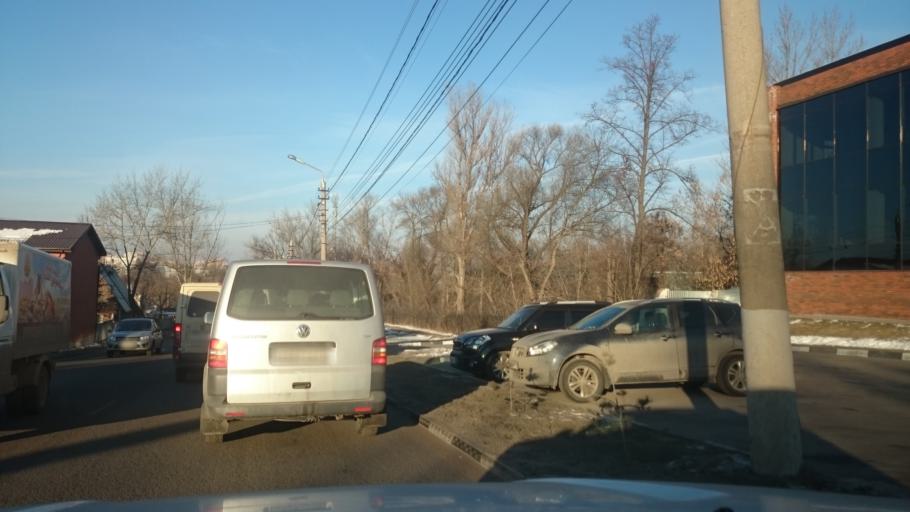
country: RU
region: Tula
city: Tula
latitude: 54.2074
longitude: 37.6503
